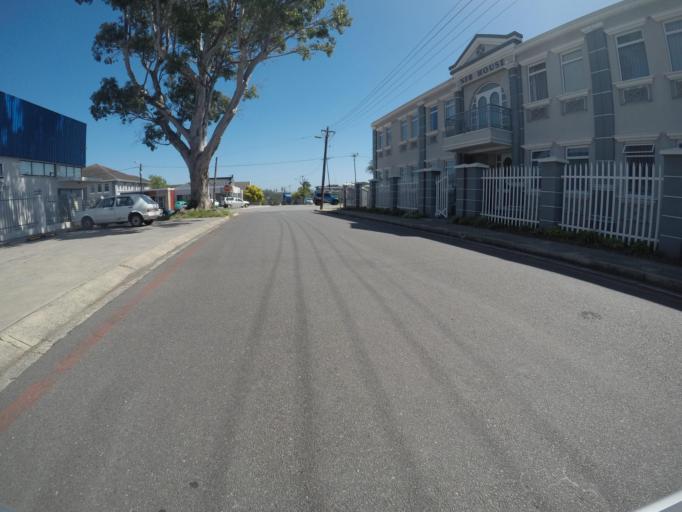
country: ZA
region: Eastern Cape
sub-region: Buffalo City Metropolitan Municipality
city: East London
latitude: -32.9850
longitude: 27.9261
